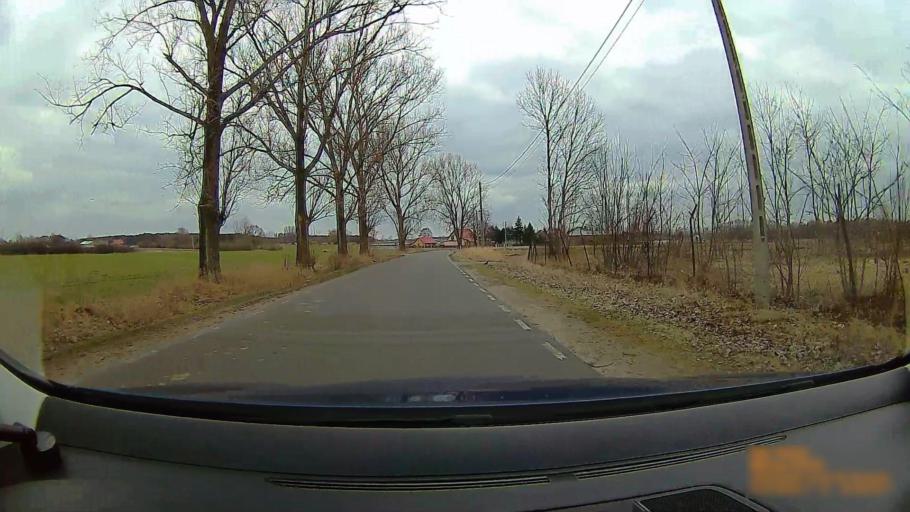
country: PL
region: Greater Poland Voivodeship
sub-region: Powiat koninski
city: Rzgow Pierwszy
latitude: 52.1480
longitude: 18.0545
